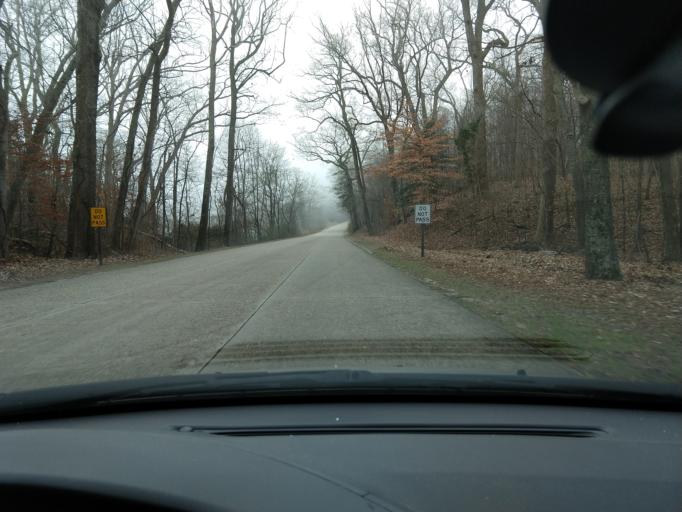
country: US
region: Virginia
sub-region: York County
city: Yorktown
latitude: 37.2444
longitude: -76.5275
